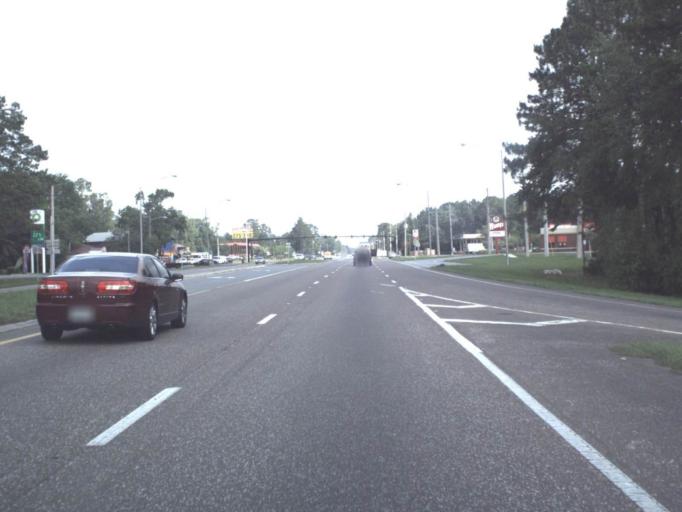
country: US
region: Florida
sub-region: Nassau County
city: Nassau Village-Ratliff
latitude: 30.4138
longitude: -81.7483
